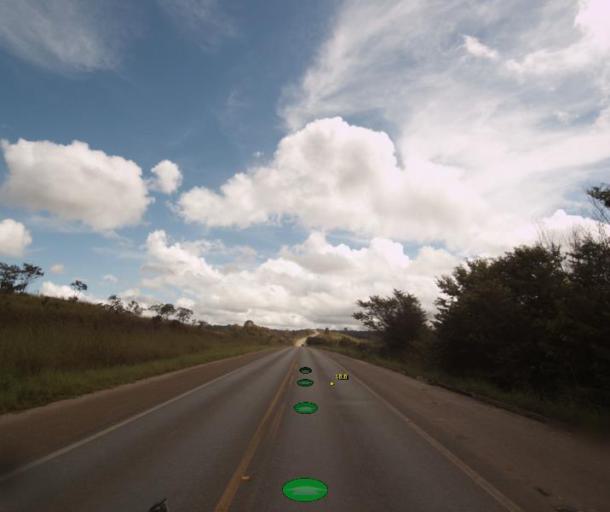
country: BR
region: Federal District
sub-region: Brasilia
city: Brasilia
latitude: -15.7435
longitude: -48.3638
